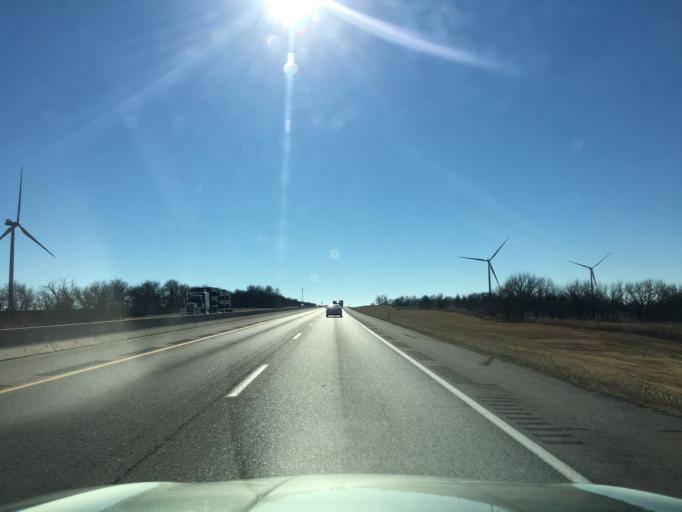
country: US
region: Kansas
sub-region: Sumner County
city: Wellington
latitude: 37.1320
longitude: -97.3390
